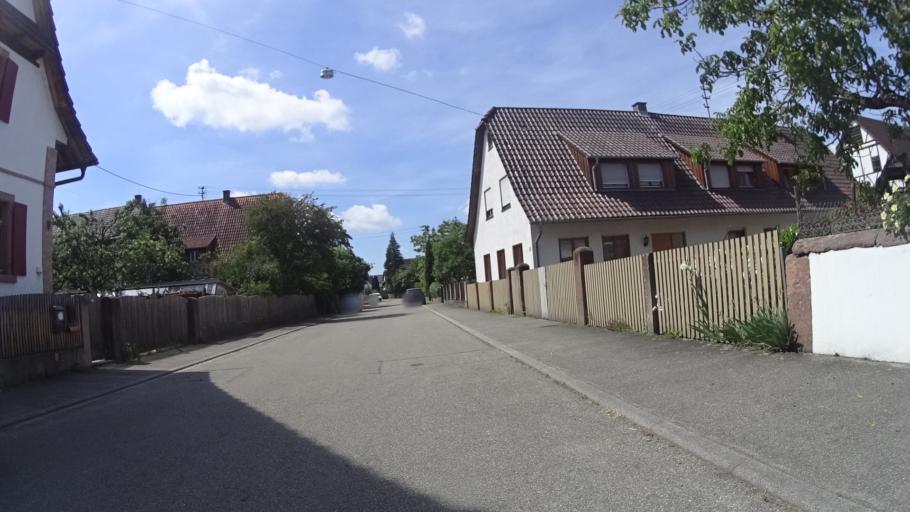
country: DE
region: Baden-Wuerttemberg
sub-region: Freiburg Region
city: Meissenheim
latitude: 48.4346
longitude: 7.8057
